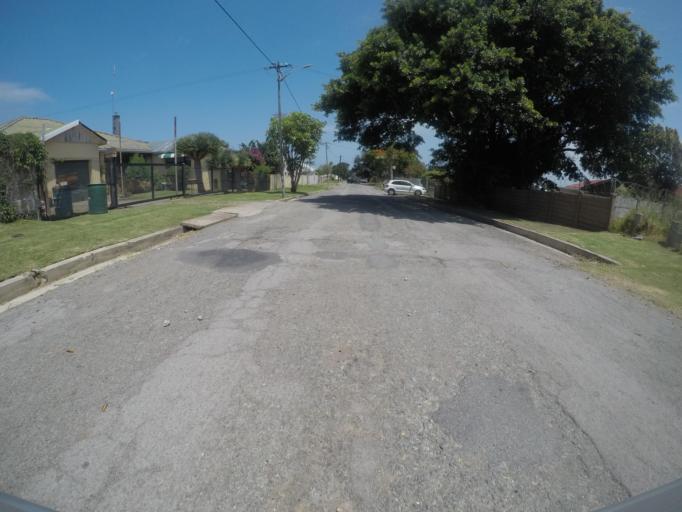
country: ZA
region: Eastern Cape
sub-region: Buffalo City Metropolitan Municipality
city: East London
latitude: -32.9739
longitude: 27.8801
